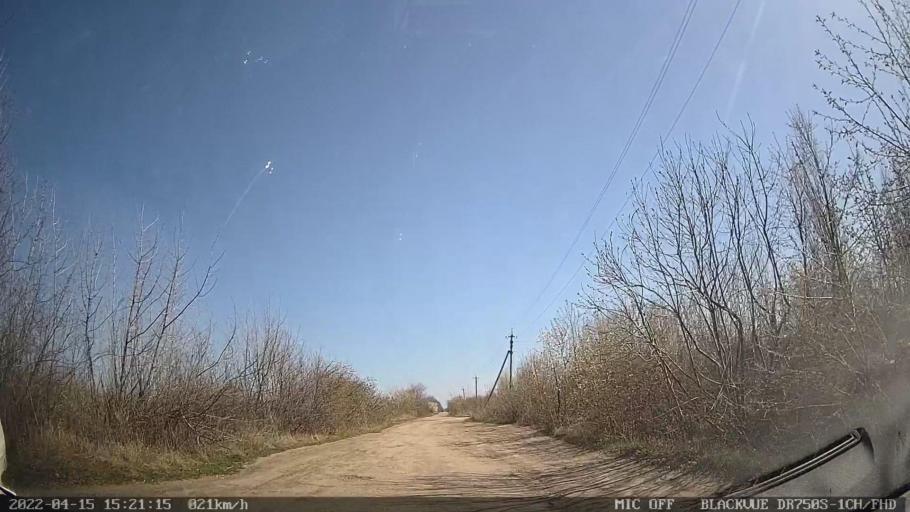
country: MD
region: Raionul Ocnita
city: Otaci
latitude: 48.3841
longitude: 27.9100
